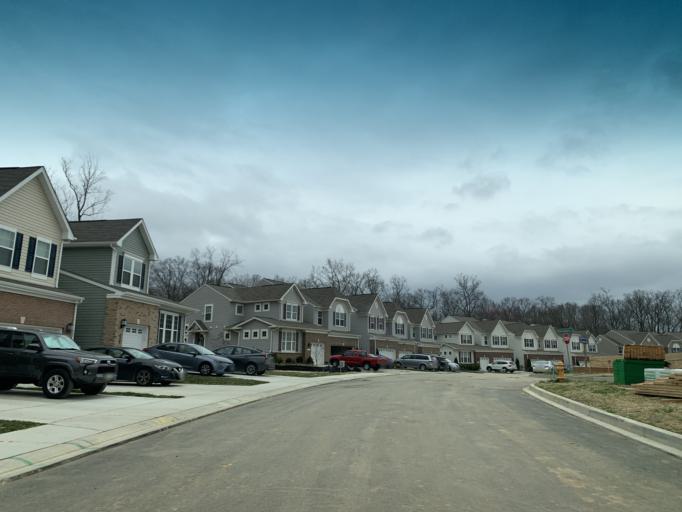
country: US
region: Maryland
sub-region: Harford County
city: Perryman
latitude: 39.4947
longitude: -76.2017
